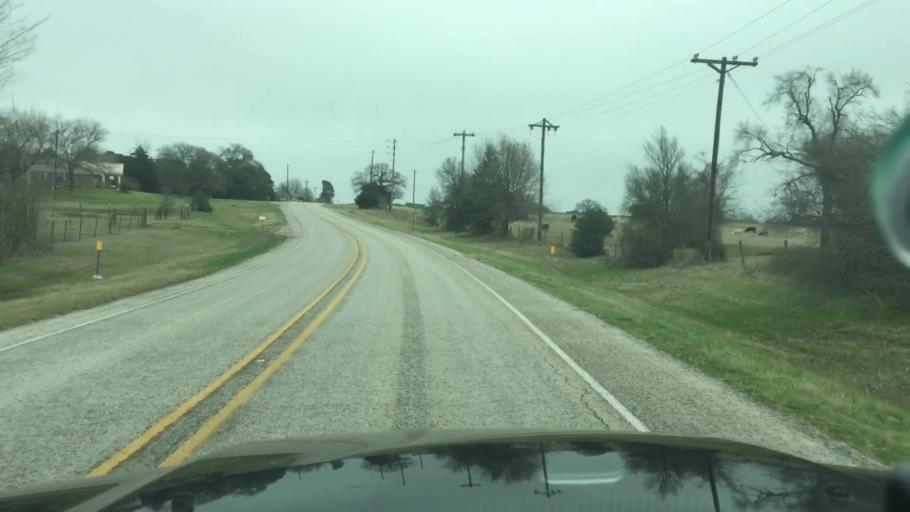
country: US
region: Texas
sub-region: Fayette County
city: La Grange
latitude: 30.0069
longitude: -96.9069
